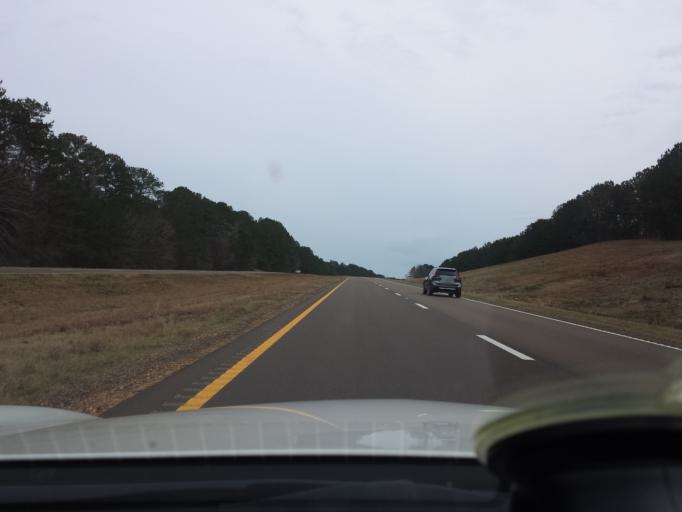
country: US
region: Mississippi
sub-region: Leake County
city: Carthage
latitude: 32.7645
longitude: -89.5719
